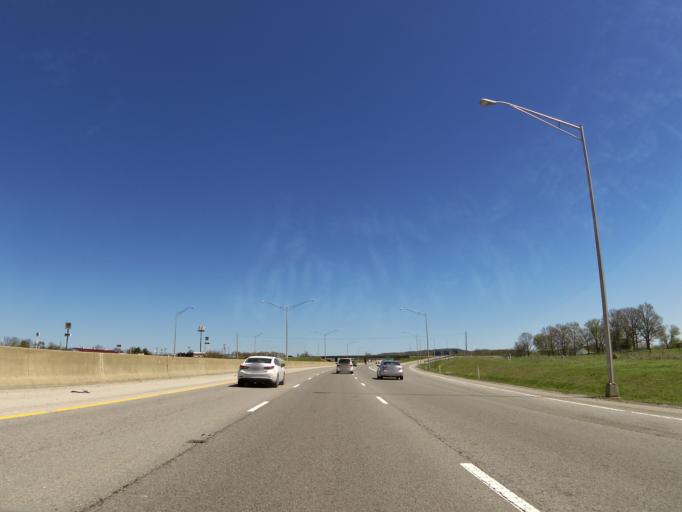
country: US
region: Kentucky
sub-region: Edmonson County
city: Brownsville
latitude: 37.0421
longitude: -86.2149
